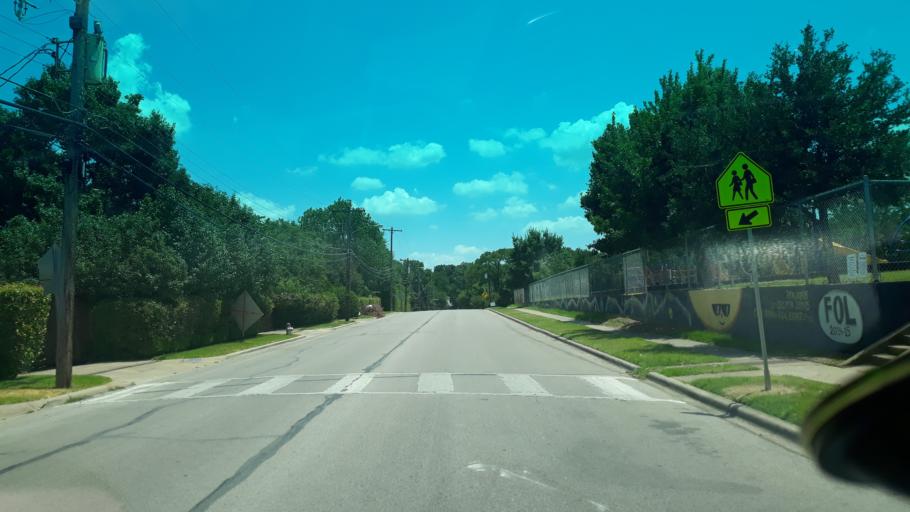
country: US
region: Texas
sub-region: Dallas County
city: Highland Park
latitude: 32.8265
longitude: -96.7431
